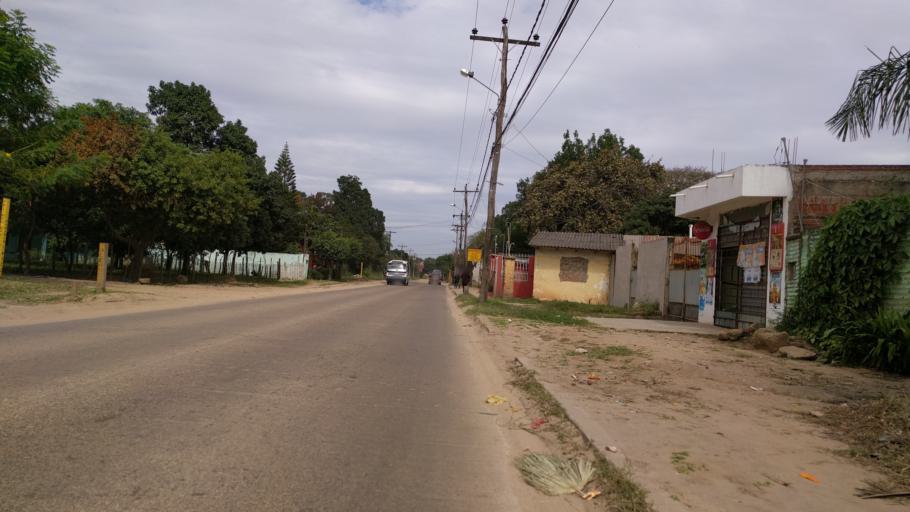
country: BO
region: Santa Cruz
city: Santa Cruz de la Sierra
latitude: -17.8220
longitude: -63.2347
